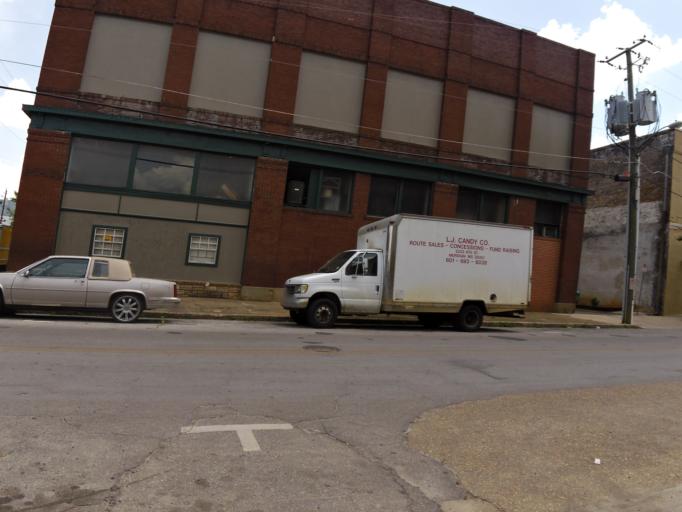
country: US
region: Mississippi
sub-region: Lauderdale County
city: Meridian
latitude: 32.3618
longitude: -88.7017
